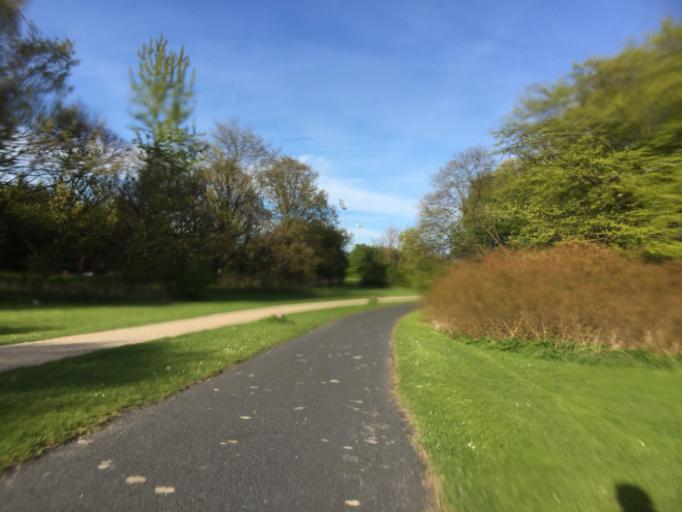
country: DK
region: Capital Region
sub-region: Kobenhavn
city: Vanlose
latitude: 55.7163
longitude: 12.4884
